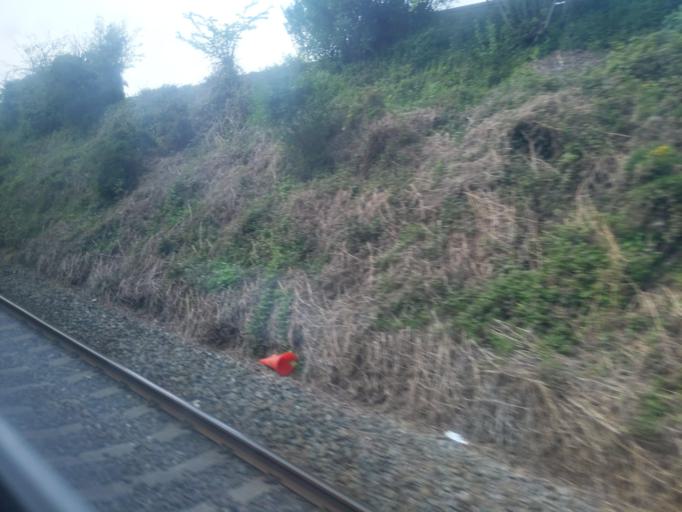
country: GB
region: England
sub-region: Cornwall
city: Redruth
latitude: 50.2255
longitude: -5.2542
